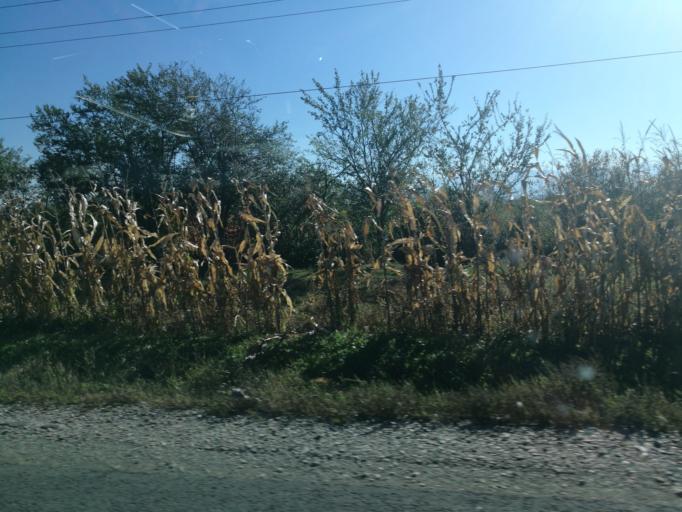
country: RO
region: Brasov
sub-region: Comuna Sercaia
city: Sercaia
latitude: 45.8307
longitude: 25.1287
